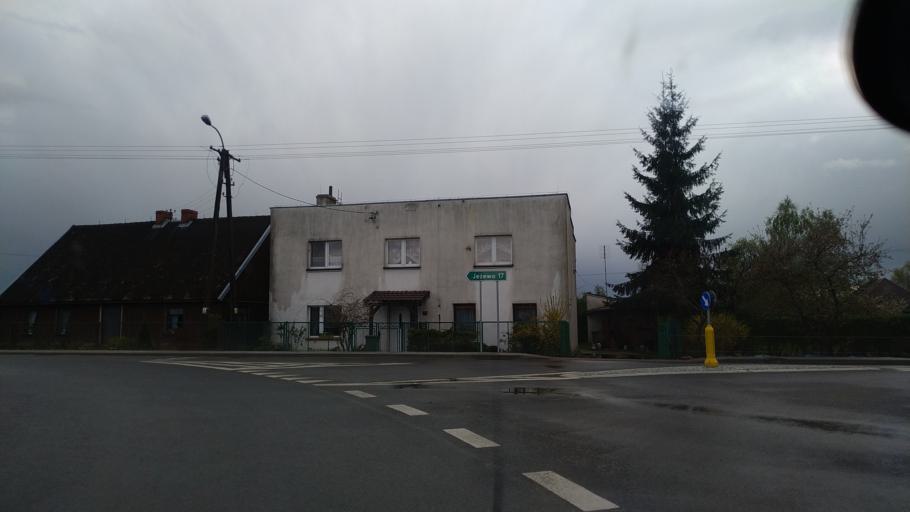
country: PL
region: Pomeranian Voivodeship
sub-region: Powiat starogardzki
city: Osiek
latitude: 53.6367
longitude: 18.4802
